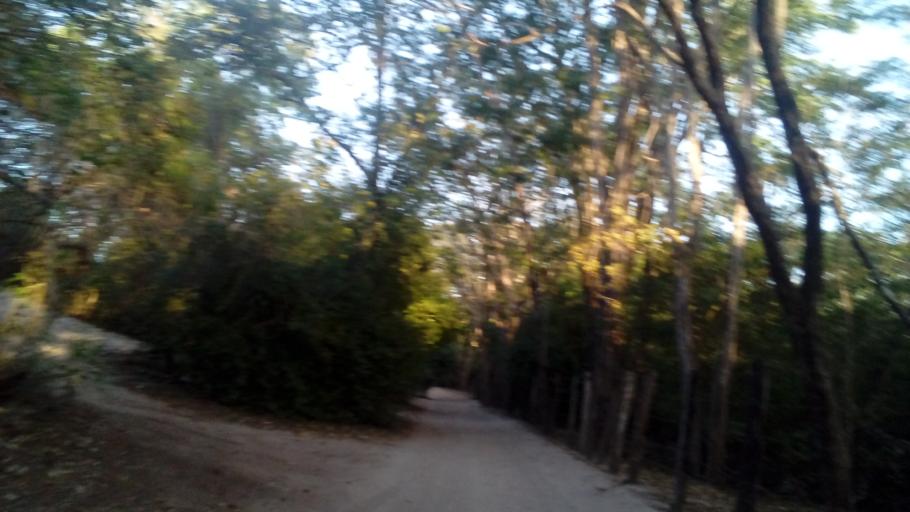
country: CR
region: Guanacaste
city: Sardinal
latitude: 10.3992
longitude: -85.8145
